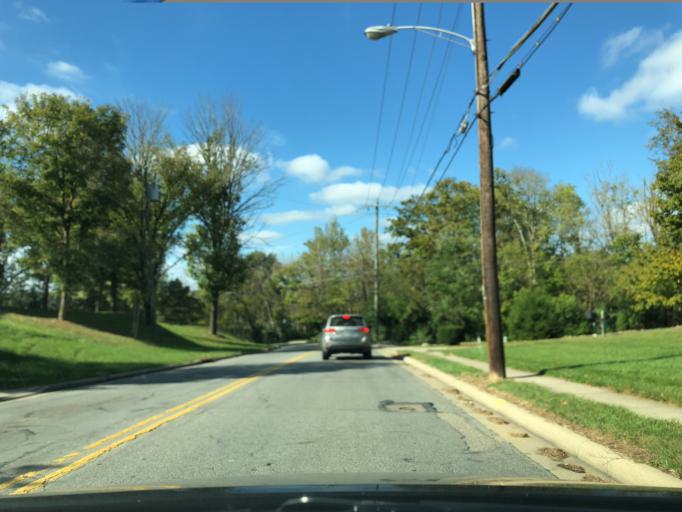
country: US
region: Ohio
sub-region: Hamilton County
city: Loveland
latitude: 39.2647
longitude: -84.2548
